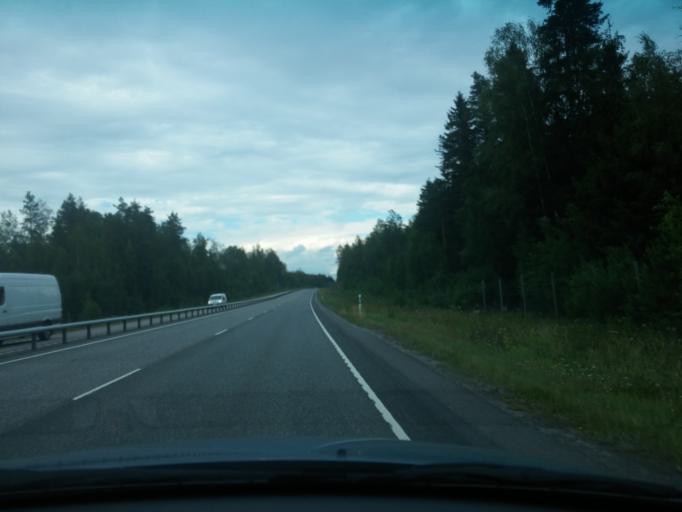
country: FI
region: Haeme
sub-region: Riihimaeki
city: Loppi
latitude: 60.7208
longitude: 24.4989
